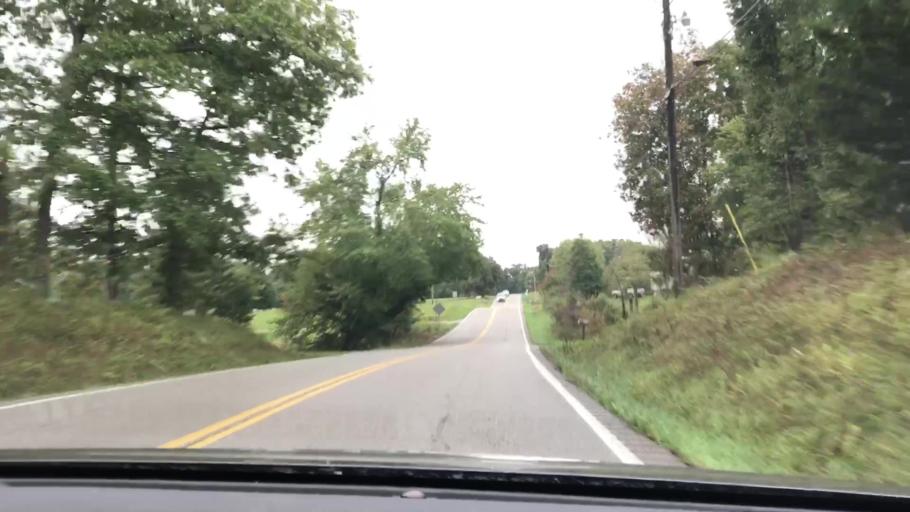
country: US
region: Tennessee
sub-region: Scott County
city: Huntsville
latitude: 36.3492
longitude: -84.6821
